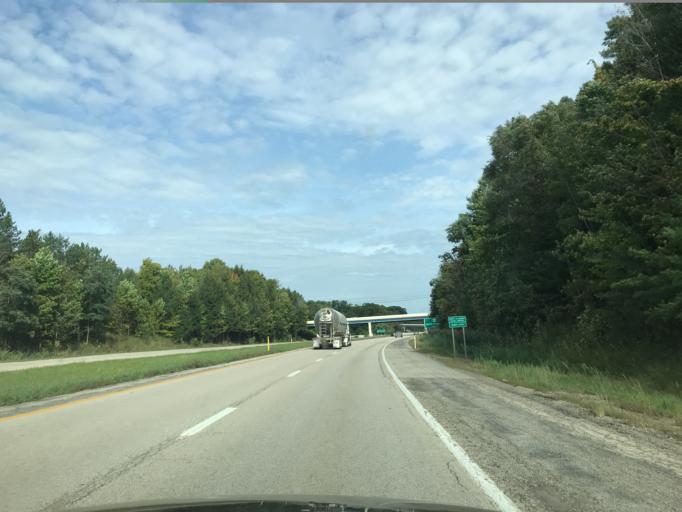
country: US
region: Ohio
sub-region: Ashtabula County
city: Edgewood
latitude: 41.8498
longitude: -80.7673
